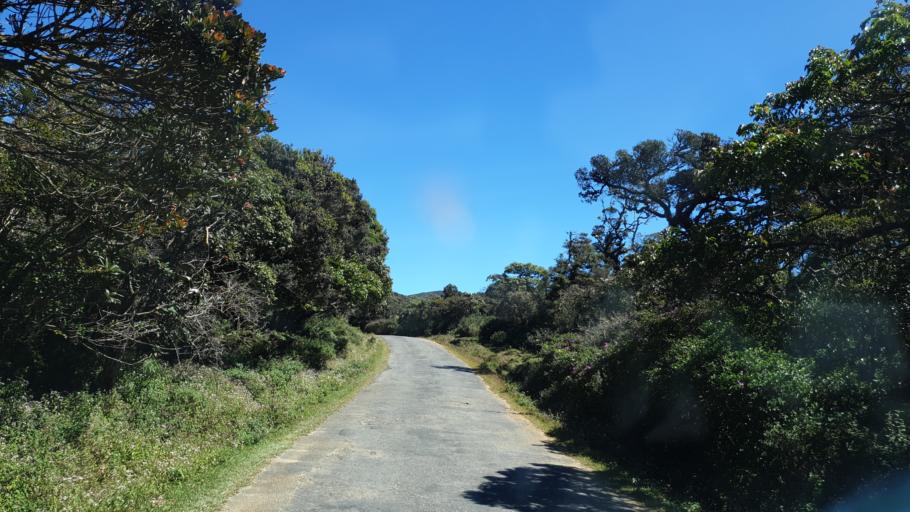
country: LK
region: Central
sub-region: Nuwara Eliya District
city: Nuwara Eliya
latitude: 6.8265
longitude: 80.8056
